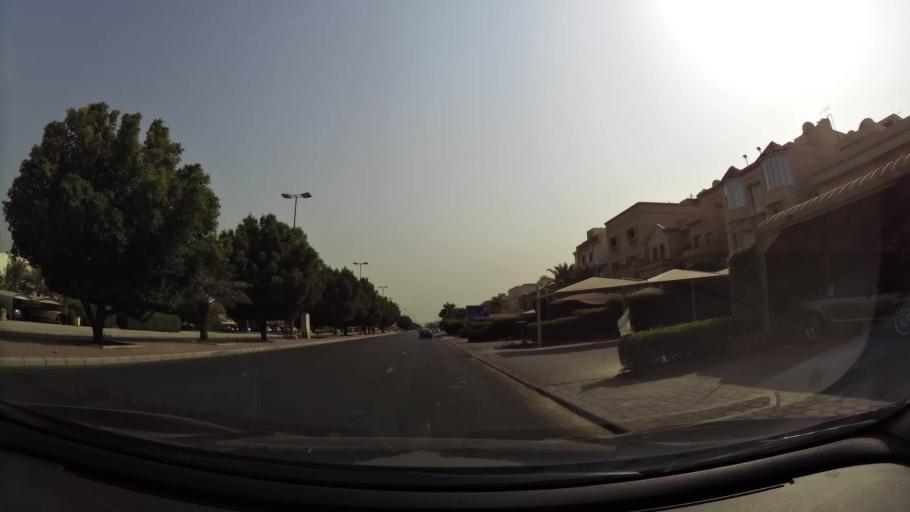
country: KW
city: Bayan
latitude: 29.2892
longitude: 48.0505
